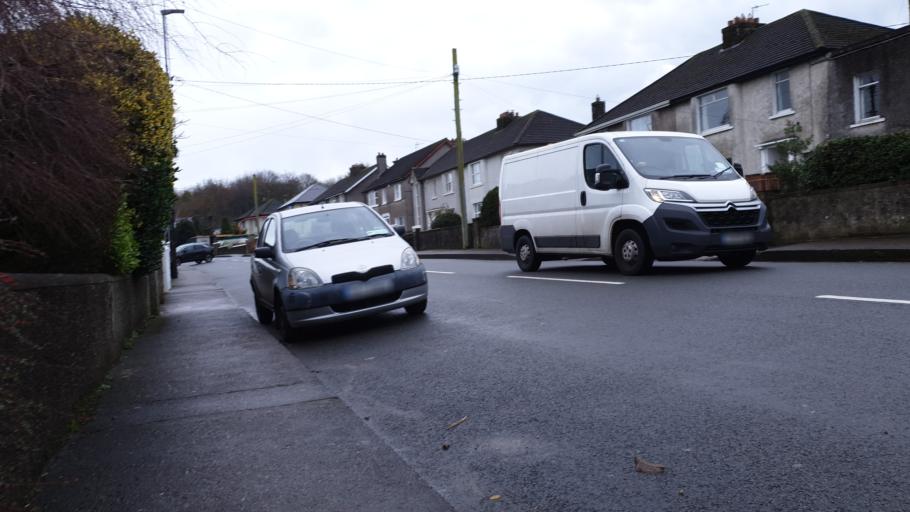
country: IE
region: Munster
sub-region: County Cork
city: Cork
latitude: 51.8940
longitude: -8.4304
